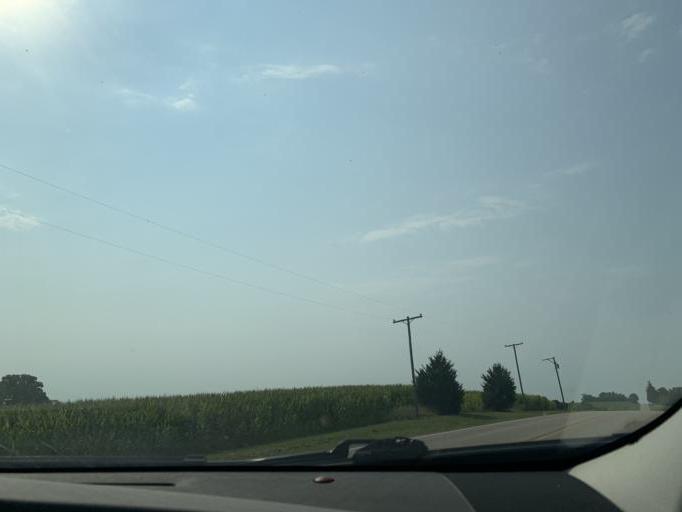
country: US
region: Illinois
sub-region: Carroll County
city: Milledgeville
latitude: 41.8478
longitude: -89.8045
